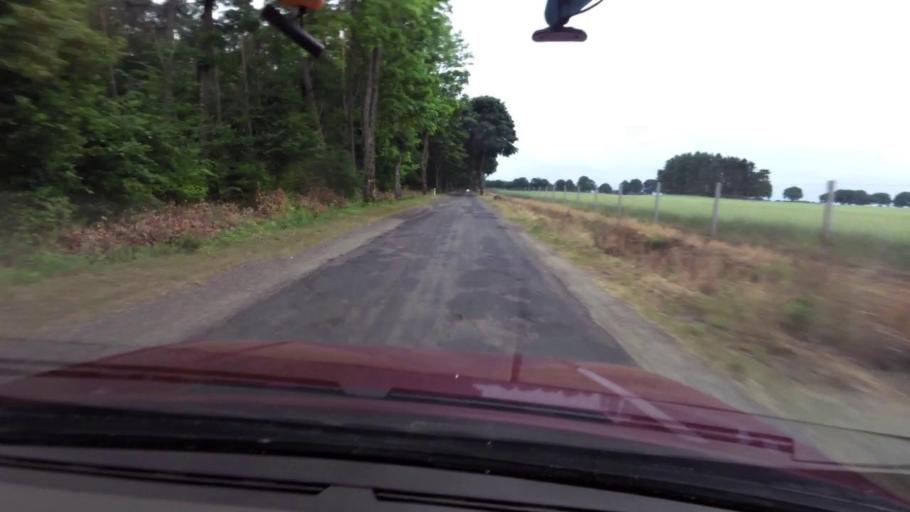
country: PL
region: Pomeranian Voivodeship
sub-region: Powiat slupski
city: Kepice
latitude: 54.2032
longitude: 16.8164
